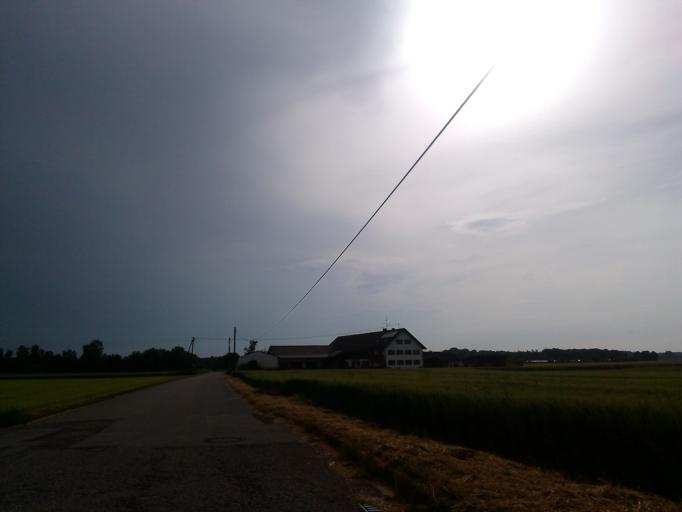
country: DE
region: Bavaria
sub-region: Upper Bavaria
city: Gilching
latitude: 48.1159
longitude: 11.2843
